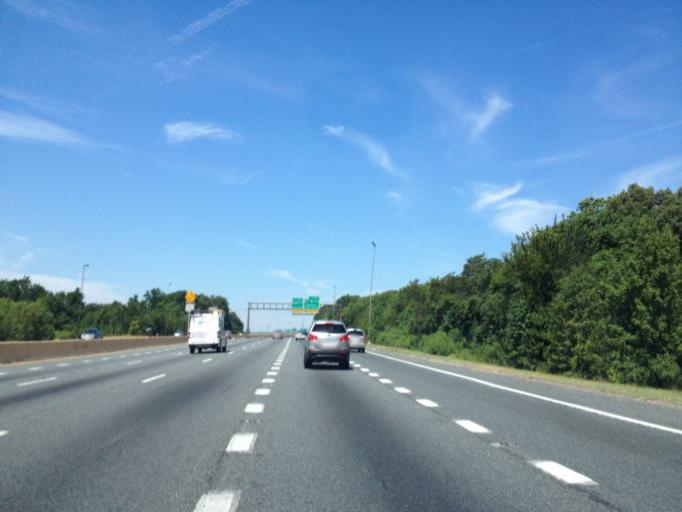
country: US
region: Maryland
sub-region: Prince George's County
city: Springdale
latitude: 38.9466
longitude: -76.8454
